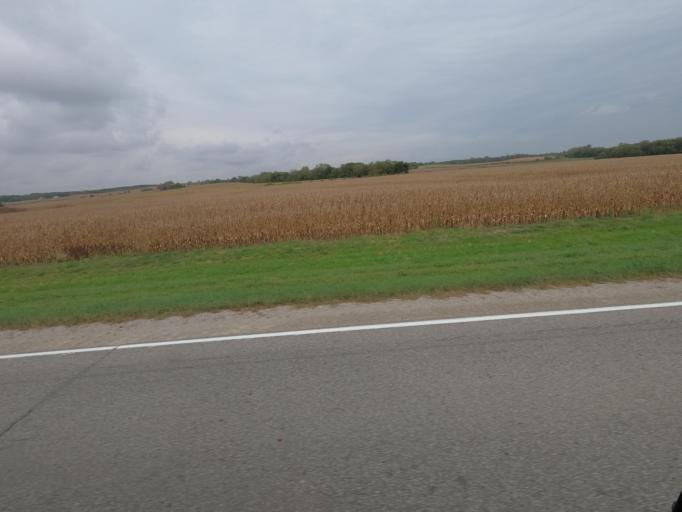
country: US
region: Iowa
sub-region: Jefferson County
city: Fairfield
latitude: 40.8970
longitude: -92.1868
